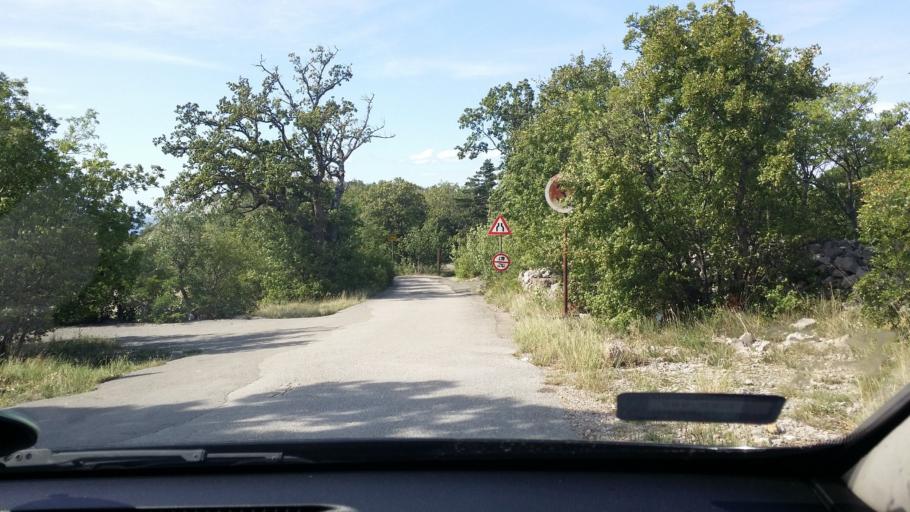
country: HR
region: Primorsko-Goranska
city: Banjol
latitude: 44.7971
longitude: 14.9013
